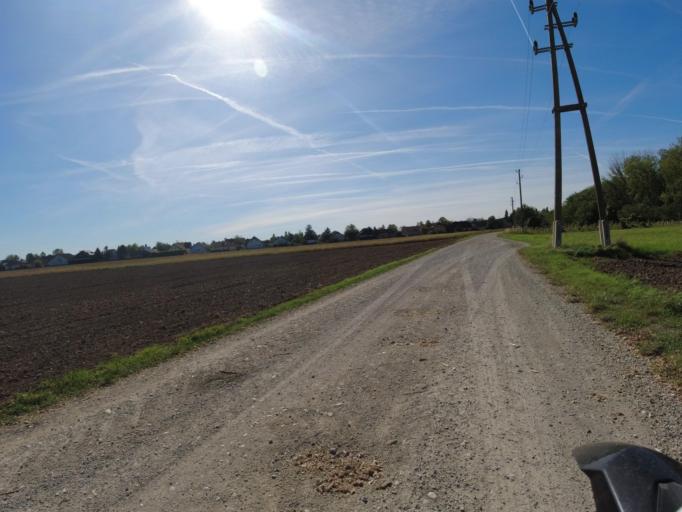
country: AT
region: Lower Austria
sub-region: Politischer Bezirk Modling
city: Guntramsdorf
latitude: 48.0227
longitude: 16.3210
